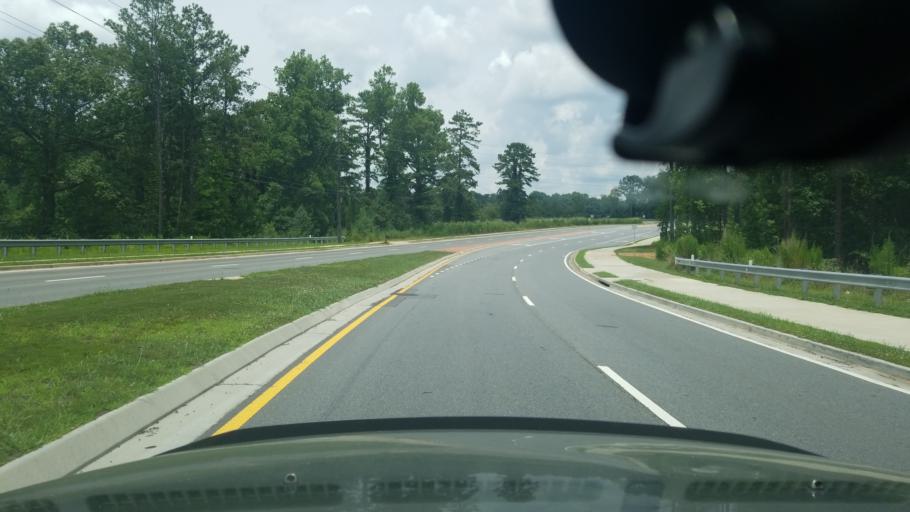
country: US
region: Georgia
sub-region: Fulton County
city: Milton
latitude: 34.1453
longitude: -84.2338
